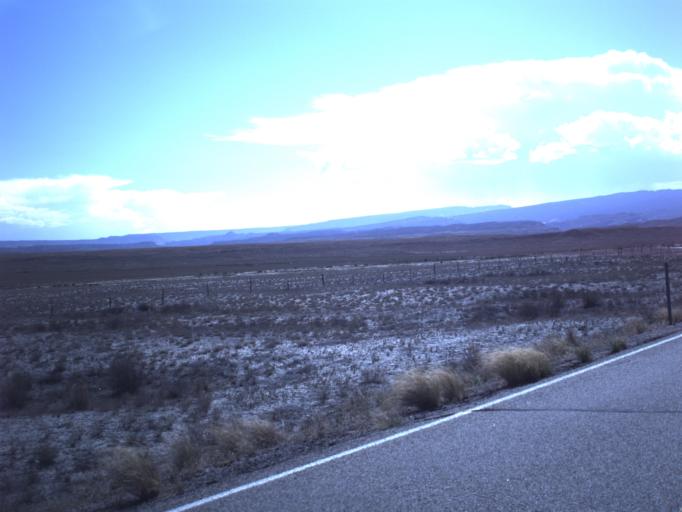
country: US
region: Utah
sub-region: Grand County
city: Moab
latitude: 38.8897
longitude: -109.3111
